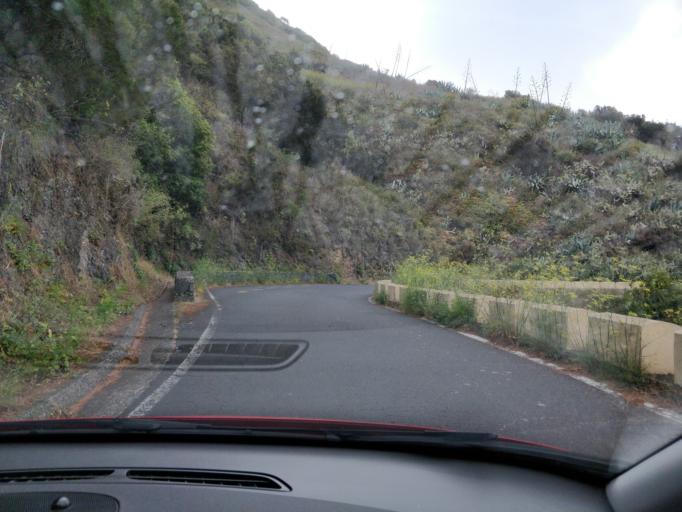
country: ES
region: Canary Islands
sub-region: Provincia de Santa Cruz de Tenerife
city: Santiago del Teide
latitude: 28.3224
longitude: -16.8492
